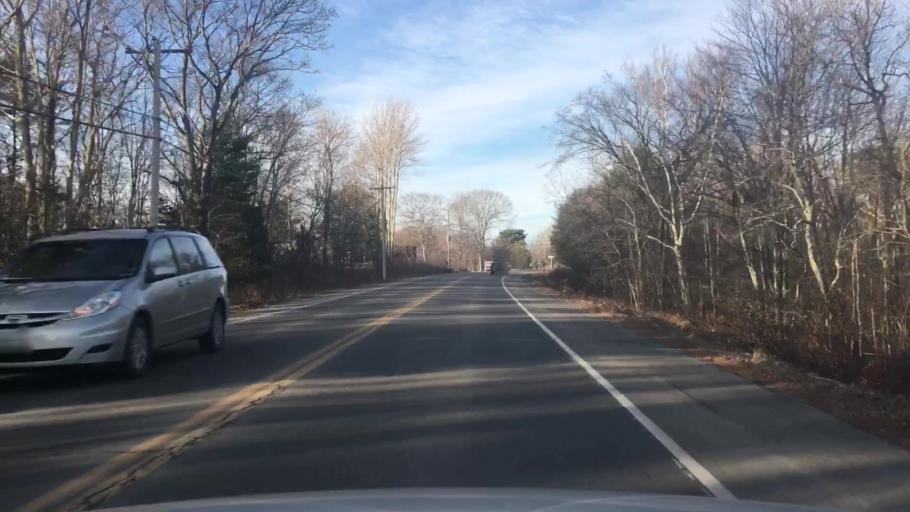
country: US
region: Maine
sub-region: Lincoln County
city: Wiscasset
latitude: 44.0312
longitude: -69.6725
